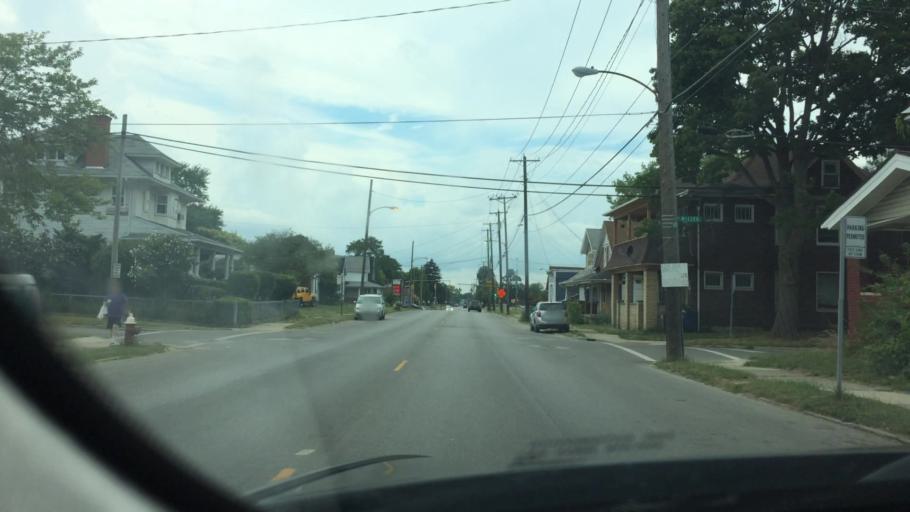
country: US
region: Ohio
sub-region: Wood County
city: Rossford
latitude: 41.6346
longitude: -83.5648
